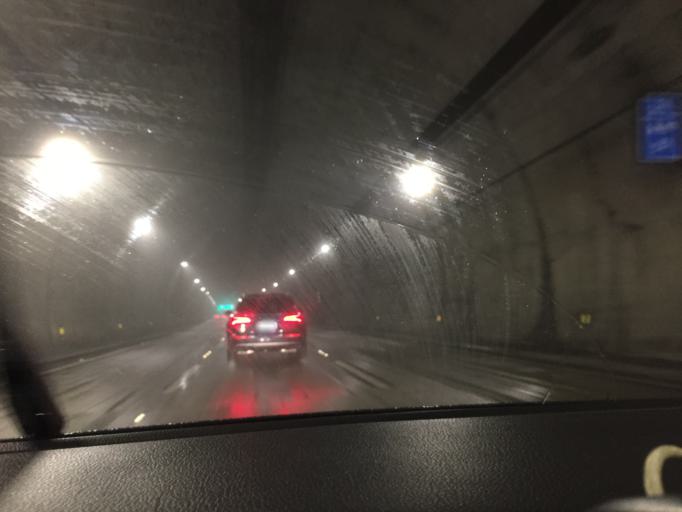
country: BR
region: Sao Paulo
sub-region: Cubatao
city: Cubatao
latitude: -23.8952
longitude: -46.5071
